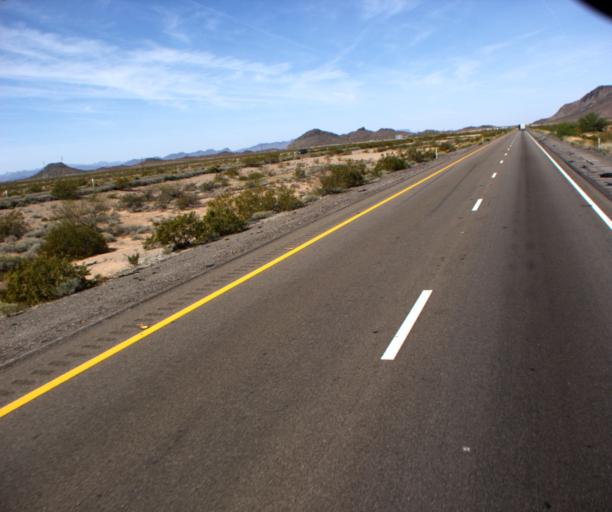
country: US
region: Arizona
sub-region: La Paz County
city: Salome
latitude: 33.6062
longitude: -113.5985
